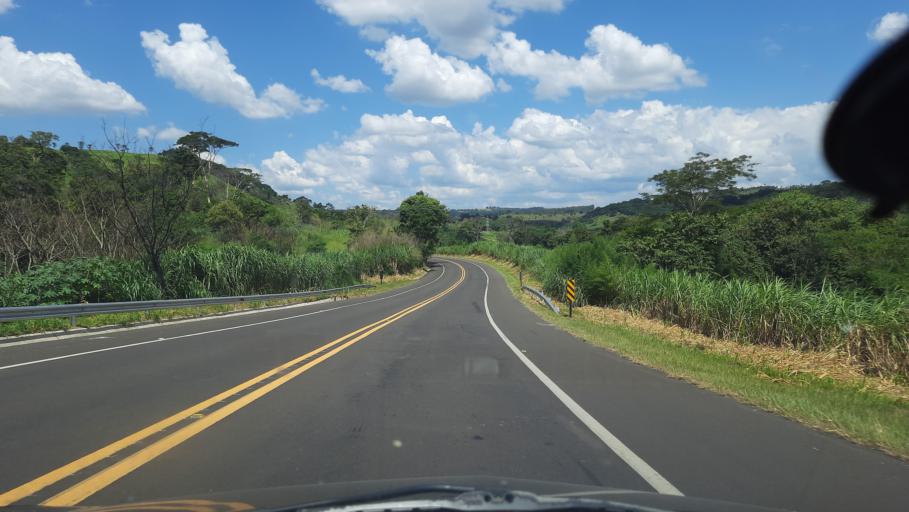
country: BR
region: Sao Paulo
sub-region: Sao Jose Do Rio Pardo
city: Sao Jose do Rio Pardo
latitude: -21.6043
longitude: -46.9732
